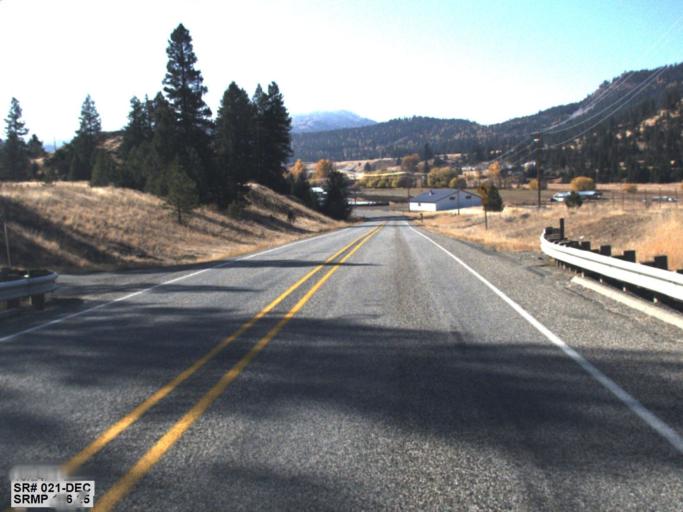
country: US
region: Washington
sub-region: Ferry County
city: Republic
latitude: 48.6914
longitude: -118.6610
